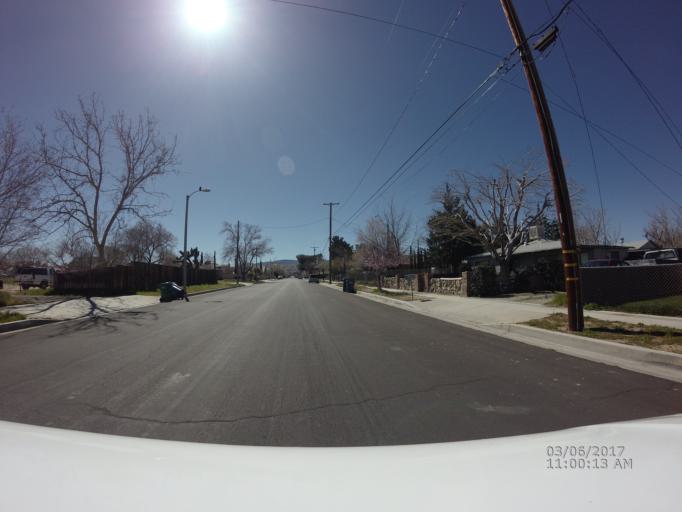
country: US
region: California
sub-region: Los Angeles County
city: Quartz Hill
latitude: 34.6574
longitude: -118.2232
